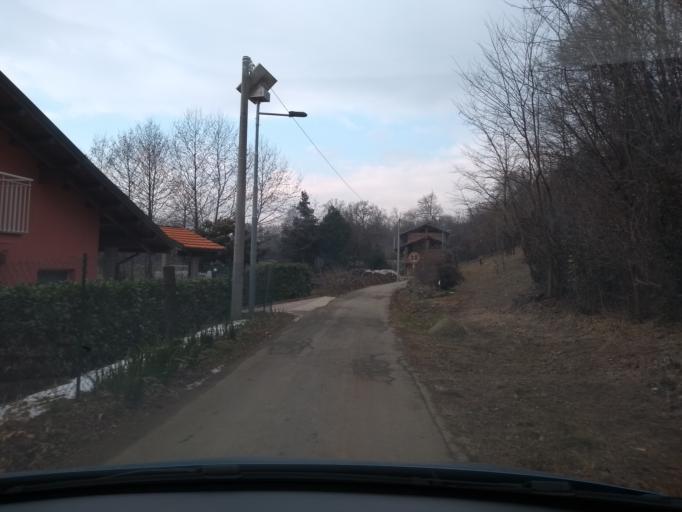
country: IT
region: Piedmont
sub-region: Provincia di Torino
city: Mathi
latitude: 45.2690
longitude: 7.5436
